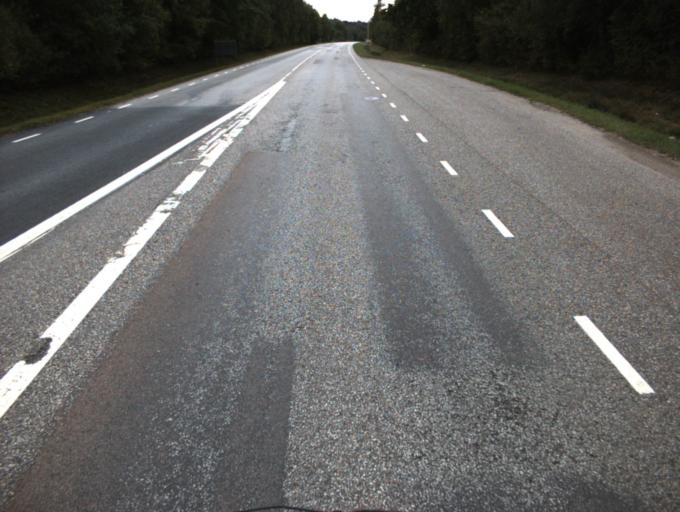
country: SE
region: Skane
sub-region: Helsingborg
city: Odakra
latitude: 56.0800
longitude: 12.7646
